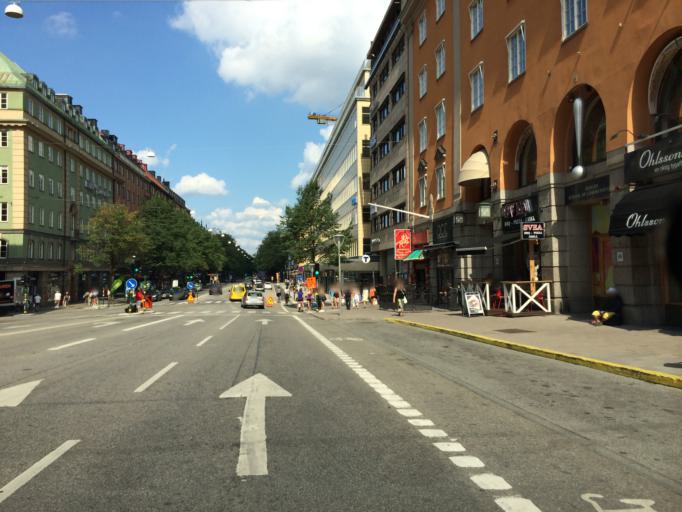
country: SE
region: Stockholm
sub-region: Stockholms Kommun
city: Stockholm
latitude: 59.3361
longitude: 18.0632
